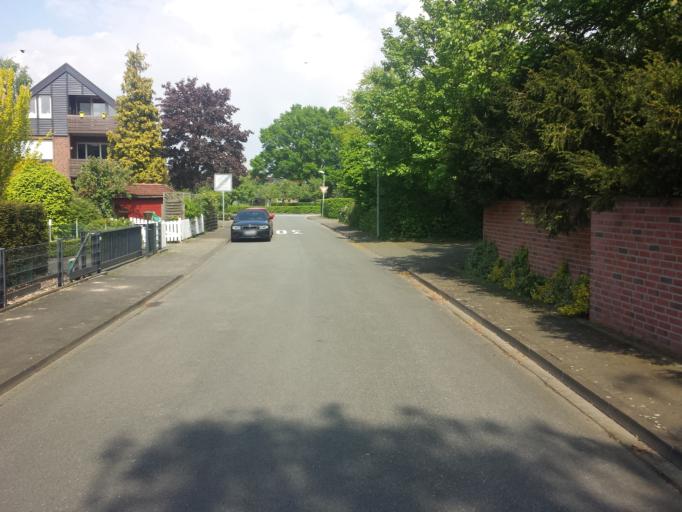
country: DE
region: North Rhine-Westphalia
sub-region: Regierungsbezirk Detmold
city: Guetersloh
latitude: 51.9031
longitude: 8.4191
